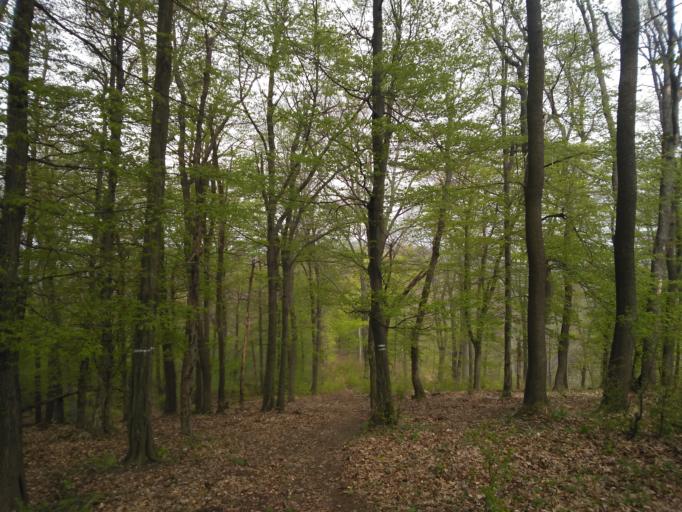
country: HU
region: Komarom-Esztergom
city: Pilismarot
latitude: 47.7451
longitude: 18.8728
